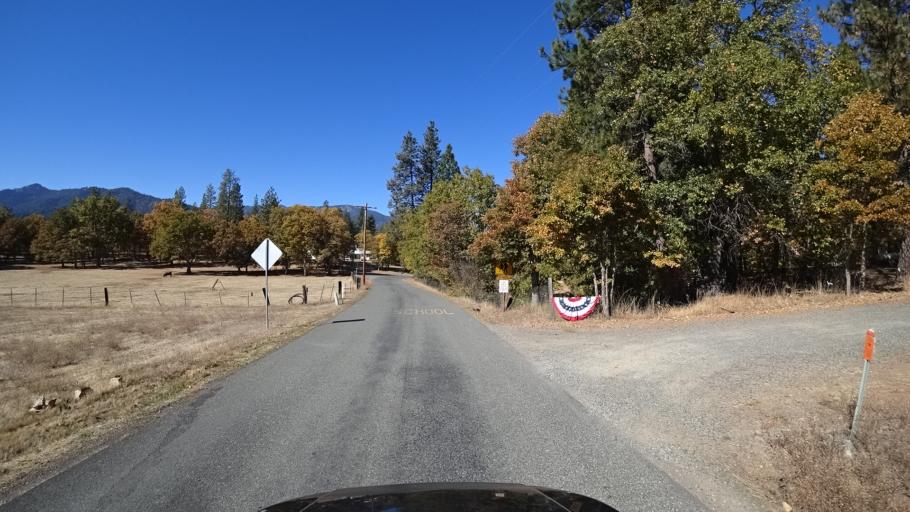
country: US
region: California
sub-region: Siskiyou County
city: Yreka
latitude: 41.5766
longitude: -122.9548
